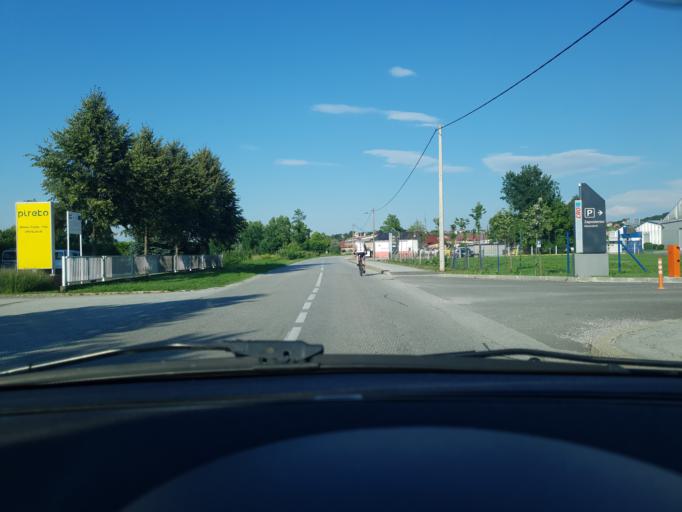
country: HR
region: Krapinsko-Zagorska
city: Oroslavje
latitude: 45.9981
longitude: 15.9217
